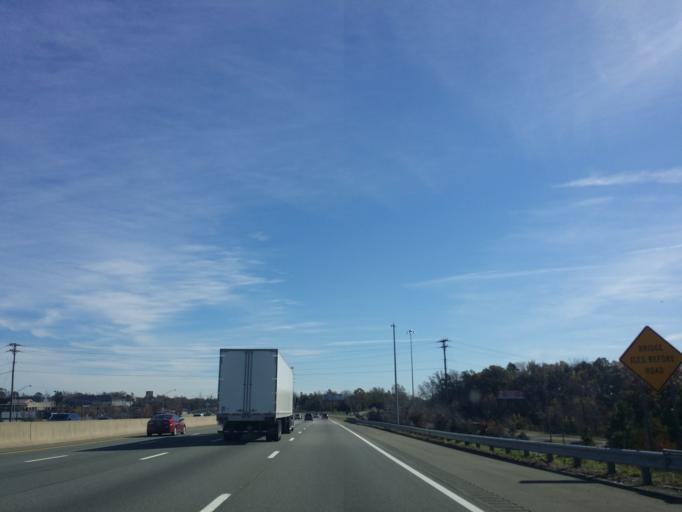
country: US
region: North Carolina
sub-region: Alamance County
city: Burlington
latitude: 36.0656
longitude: -79.4704
